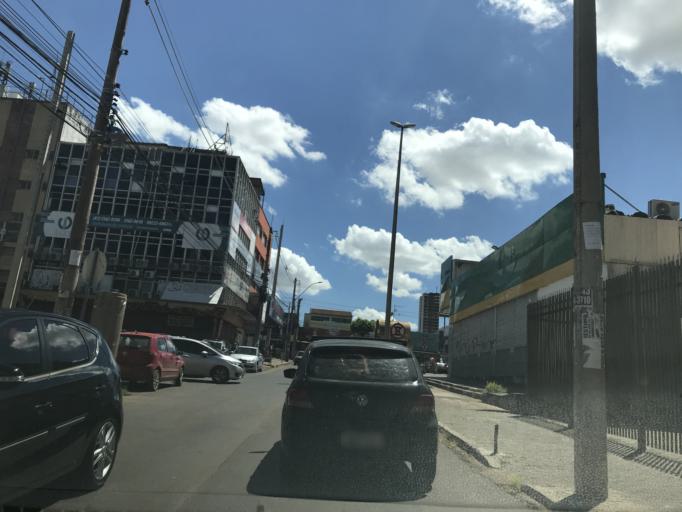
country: BR
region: Federal District
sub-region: Brasilia
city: Brasilia
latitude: -15.8353
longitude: -48.0574
